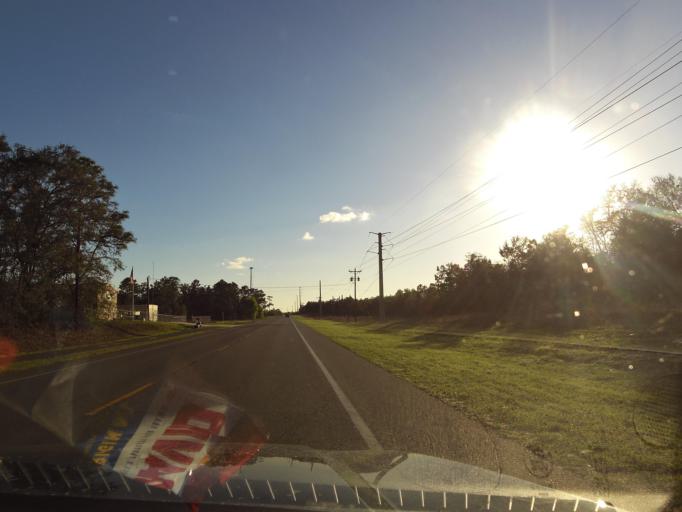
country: US
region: Florida
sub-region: Clay County
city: Keystone Heights
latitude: 29.8117
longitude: -82.0062
